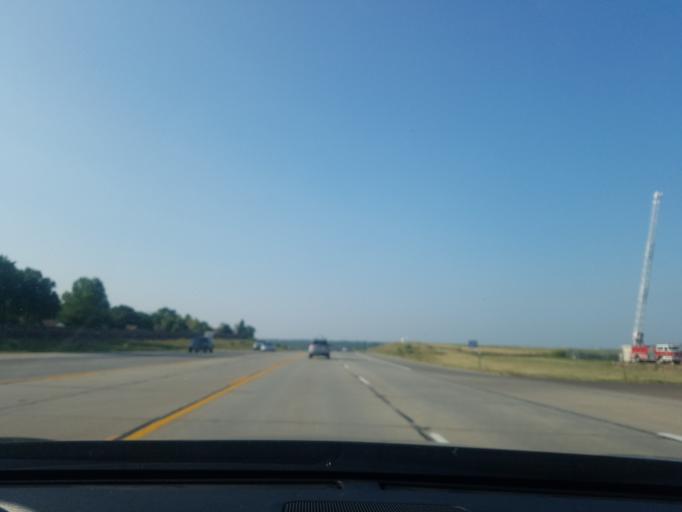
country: US
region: Colorado
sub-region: Larimer County
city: Campion
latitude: 40.3665
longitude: -105.0731
